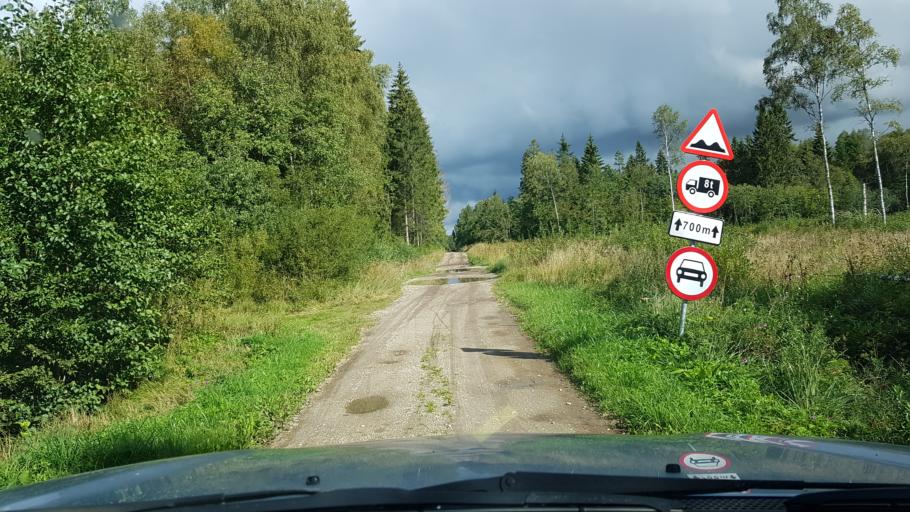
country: EE
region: Harju
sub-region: Raasiku vald
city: Arukula
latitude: 59.3149
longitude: 25.0753
